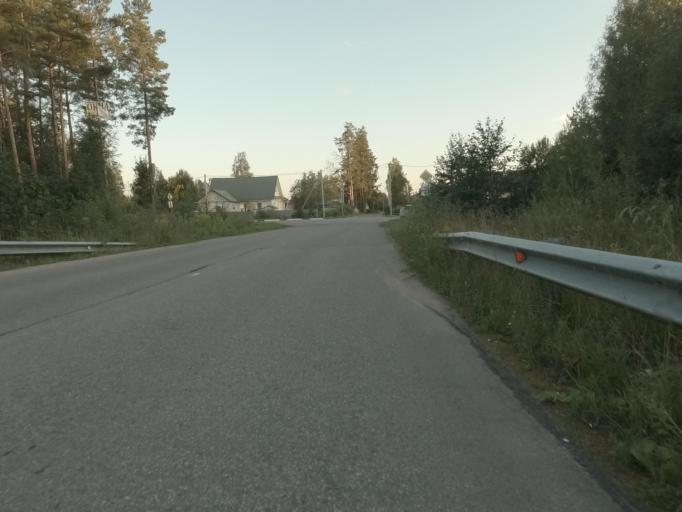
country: RU
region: Leningrad
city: Mga
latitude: 59.7611
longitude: 31.0404
